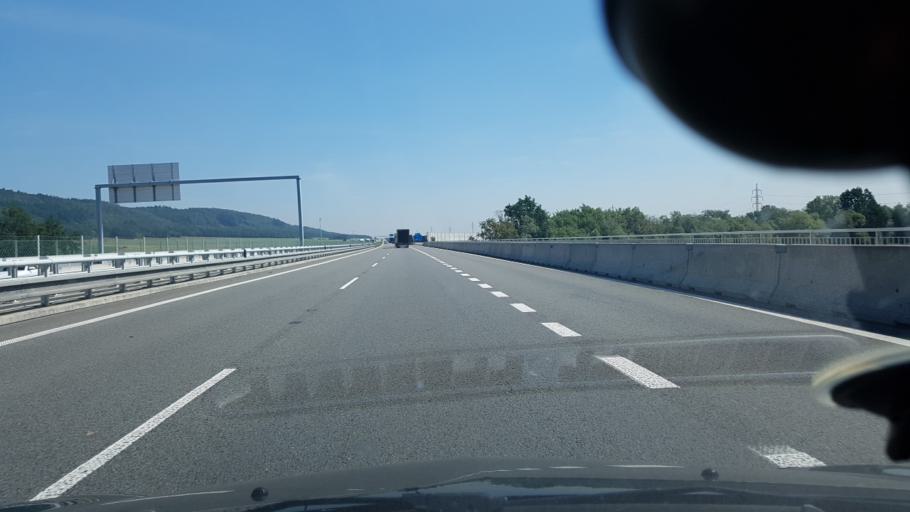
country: CZ
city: Odry
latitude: 49.6387
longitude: 17.8641
